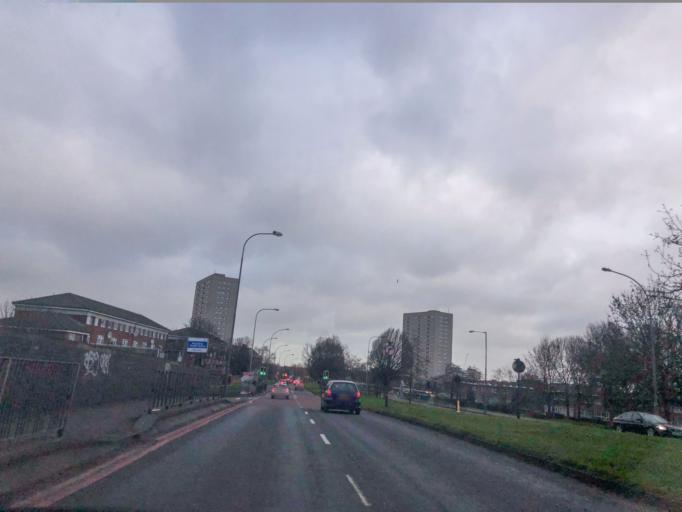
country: GB
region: England
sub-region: City and Borough of Birmingham
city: Hockley
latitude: 52.4816
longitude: -1.9242
